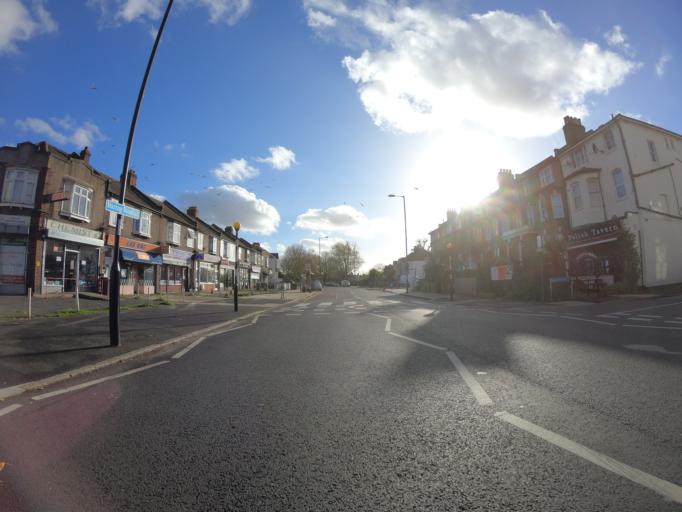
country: GB
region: England
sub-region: Greater London
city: Blackheath
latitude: 51.4434
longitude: 0.0151
